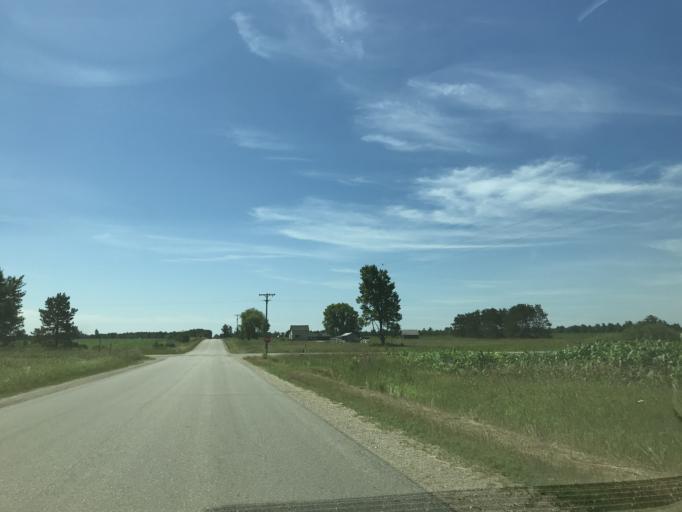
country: US
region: Michigan
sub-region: Missaukee County
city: Lake City
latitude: 44.2803
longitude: -85.0743
